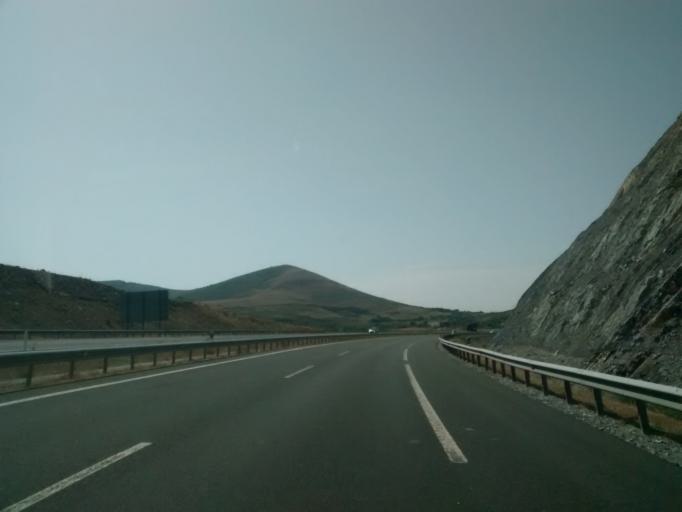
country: ES
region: Cantabria
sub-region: Provincia de Cantabria
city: Villaescusa
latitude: 42.9345
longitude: -4.1230
